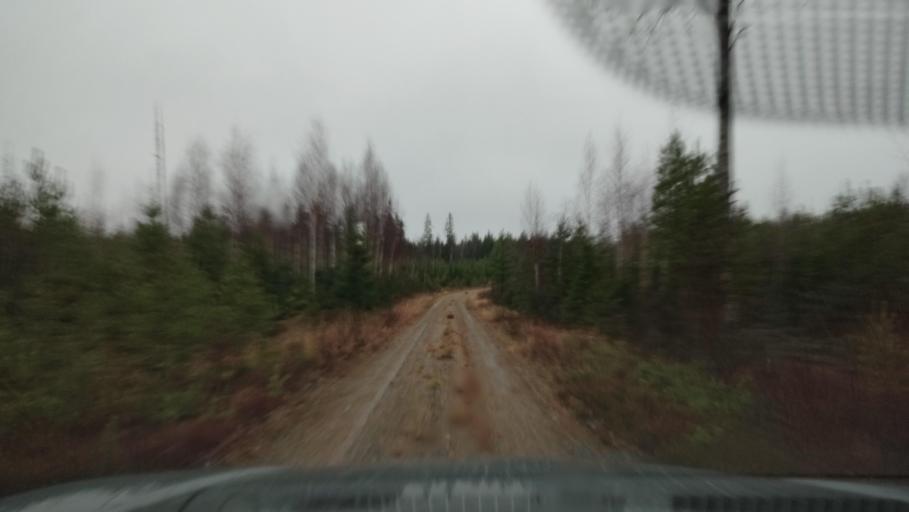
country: FI
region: Southern Ostrobothnia
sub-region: Suupohja
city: Karijoki
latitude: 62.1494
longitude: 21.5910
